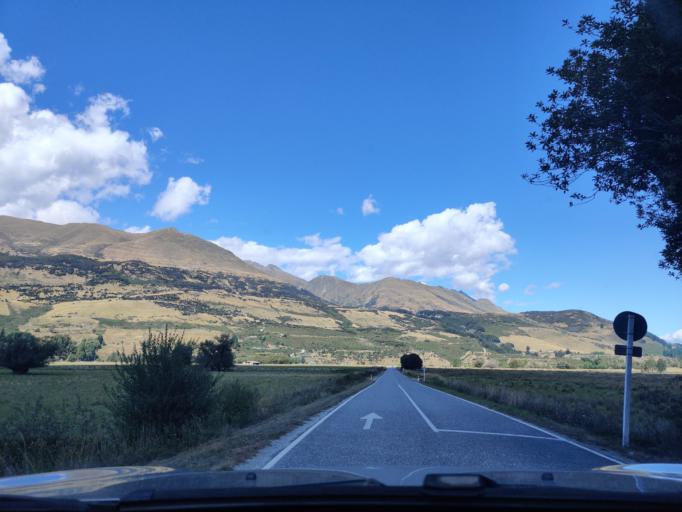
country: NZ
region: Otago
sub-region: Queenstown-Lakes District
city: Queenstown
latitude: -44.7882
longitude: 168.3975
